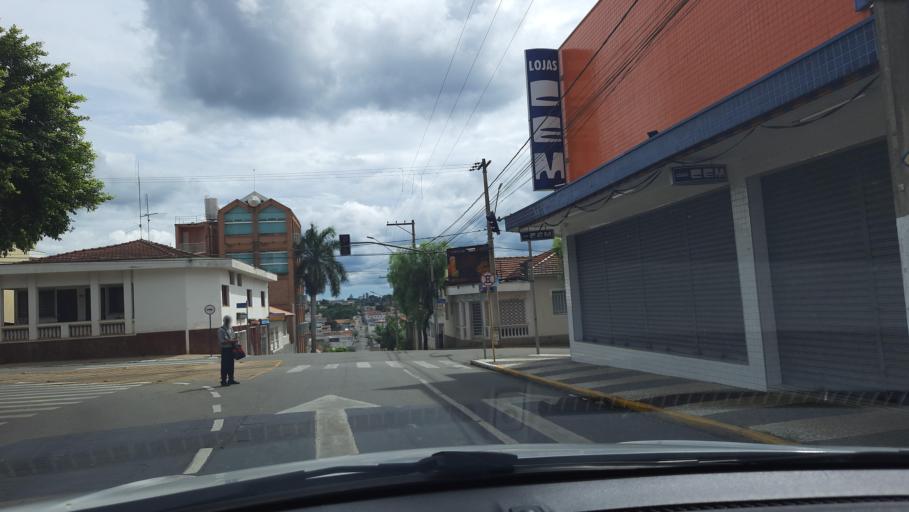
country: BR
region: Sao Paulo
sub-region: Vargem Grande Do Sul
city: Vargem Grande do Sul
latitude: -21.8317
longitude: -46.8943
